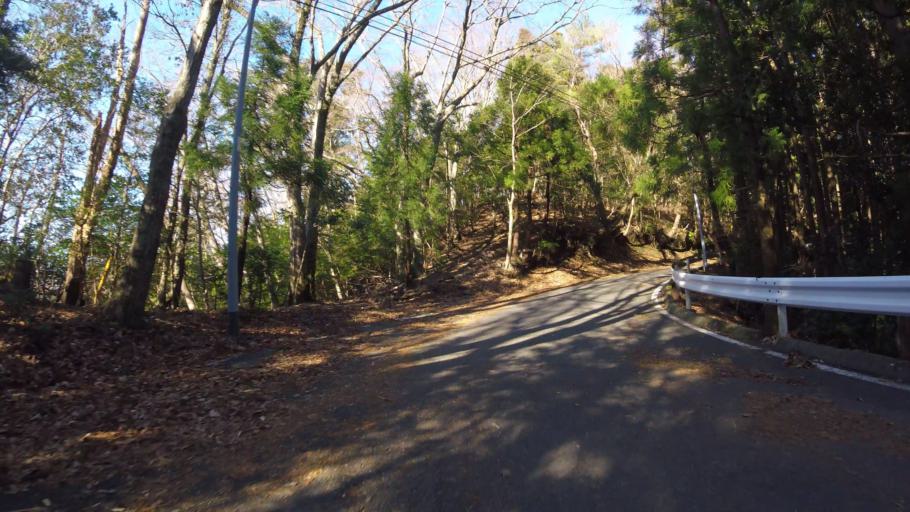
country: JP
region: Shizuoka
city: Ito
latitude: 34.8951
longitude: 138.9511
